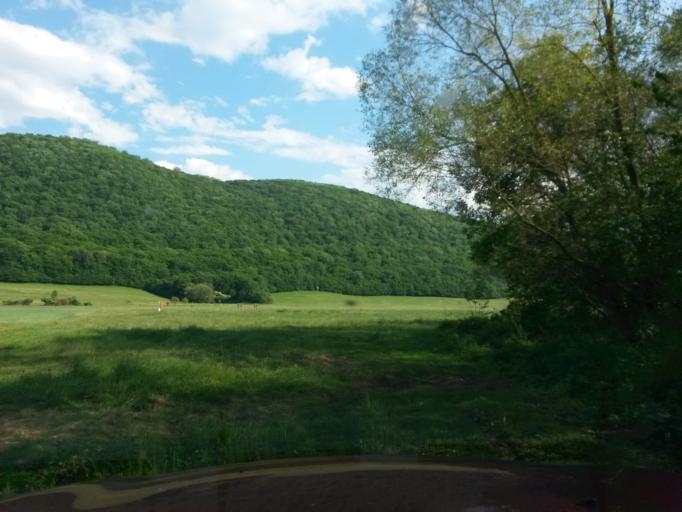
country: SK
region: Kosicky
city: Roznava
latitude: 48.5721
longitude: 20.6439
